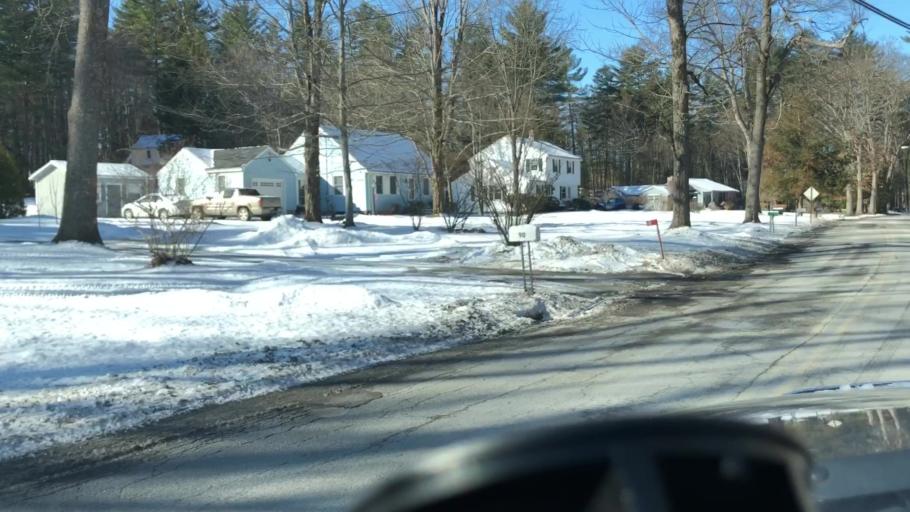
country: US
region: Massachusetts
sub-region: Hampshire County
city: Southampton
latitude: 42.2214
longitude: -72.7131
